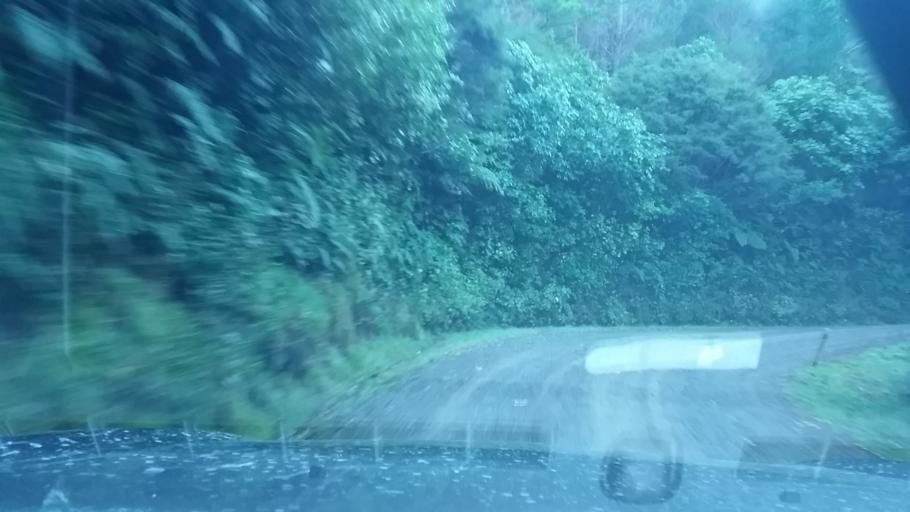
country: NZ
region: Marlborough
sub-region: Marlborough District
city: Picton
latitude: -41.1376
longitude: 174.0541
